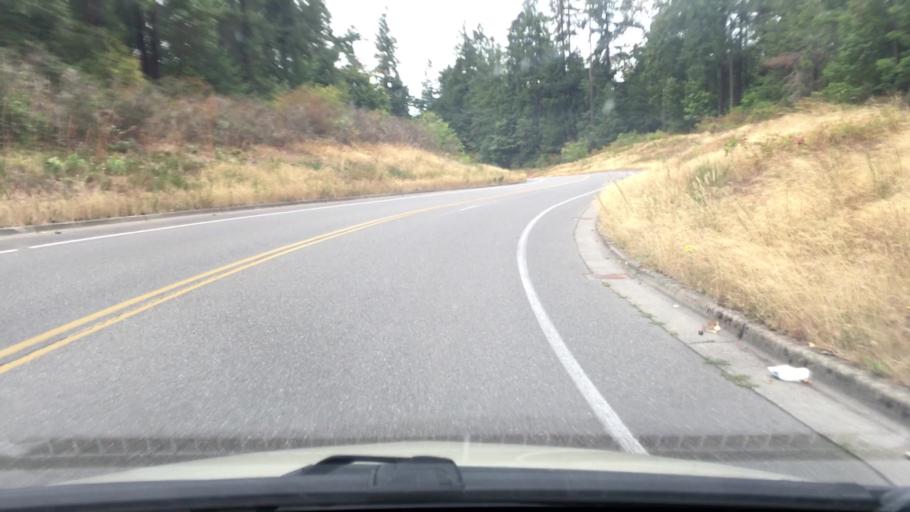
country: US
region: Washington
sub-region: Pierce County
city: Fort Lewis
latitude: 47.1084
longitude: -122.5901
